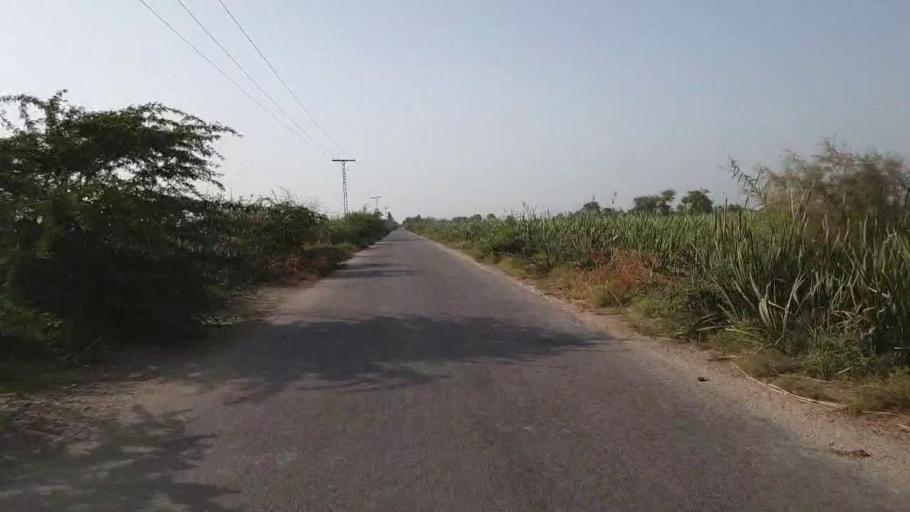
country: PK
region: Sindh
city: Jam Sahib
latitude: 26.3995
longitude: 68.8782
